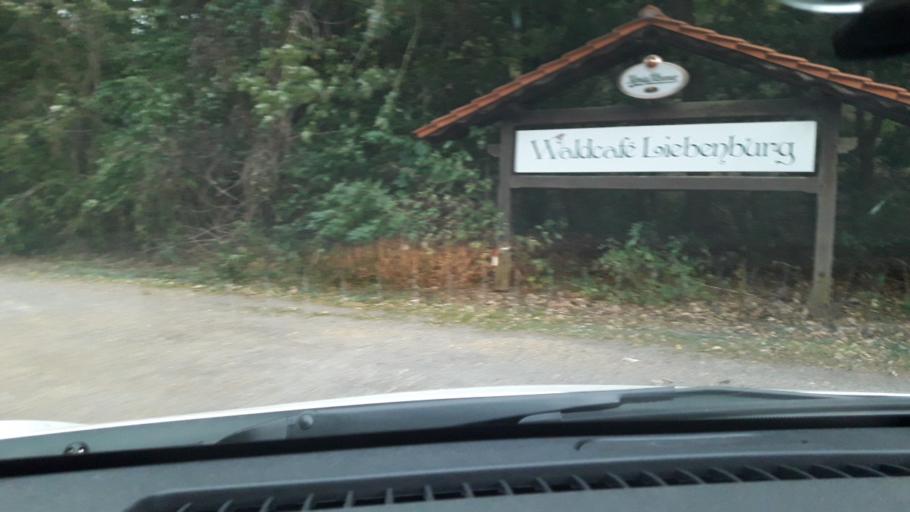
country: DE
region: Lower Saxony
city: Liebenburg
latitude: 52.0175
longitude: 10.4228
